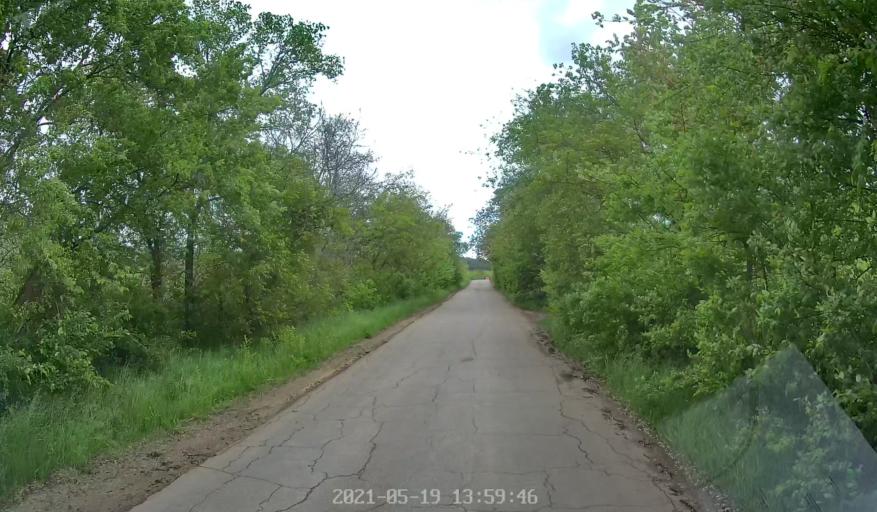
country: MD
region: Chisinau
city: Chisinau
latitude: 47.0386
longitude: 28.9264
